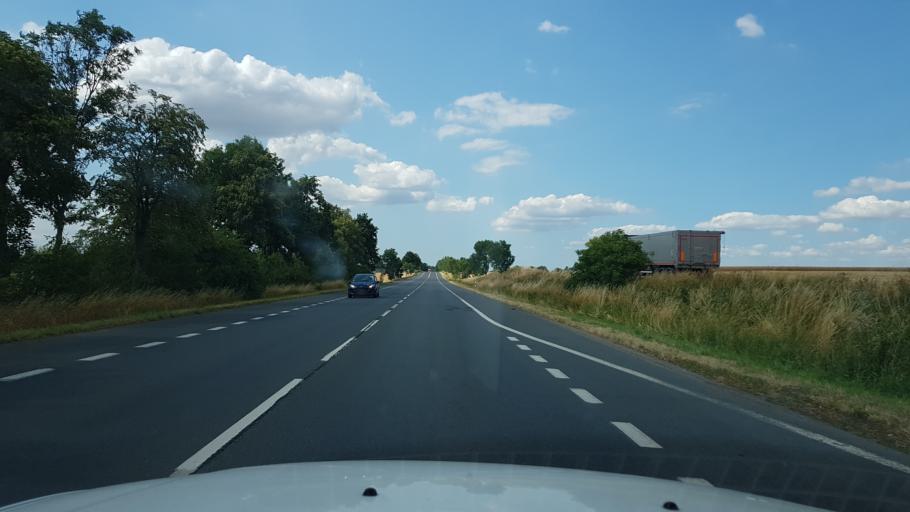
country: PL
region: West Pomeranian Voivodeship
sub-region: Powiat pyrzycki
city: Pyrzyce
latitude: 53.1116
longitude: 14.8953
